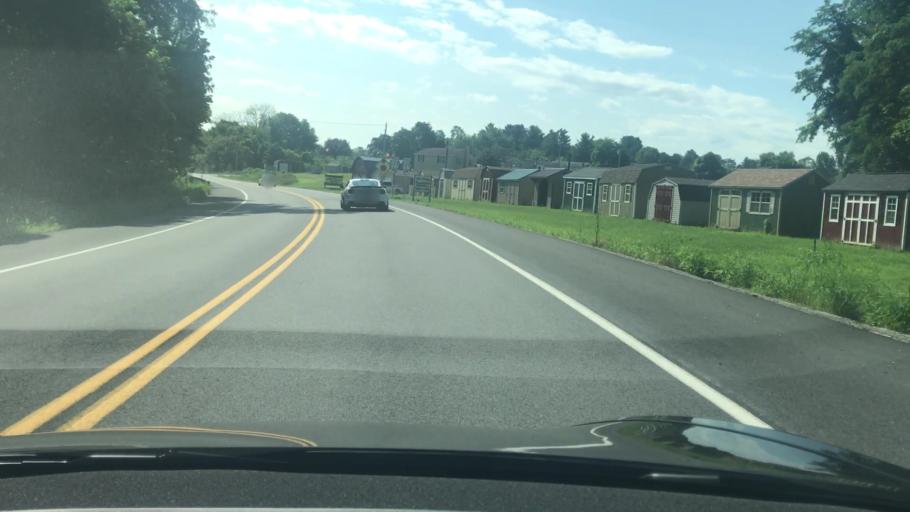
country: US
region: Pennsylvania
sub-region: York County
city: Valley Green
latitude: 40.1336
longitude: -76.8645
